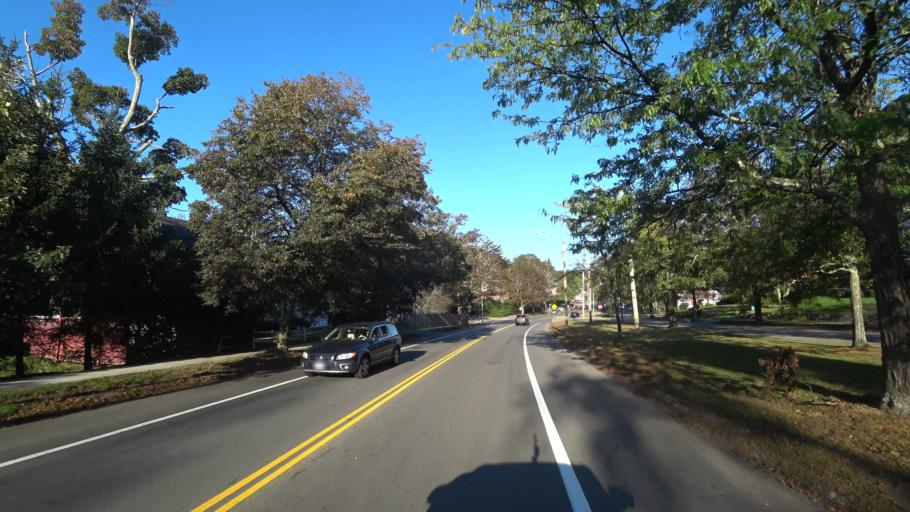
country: US
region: Massachusetts
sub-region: Middlesex County
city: Newton
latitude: 42.3397
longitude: -71.2362
